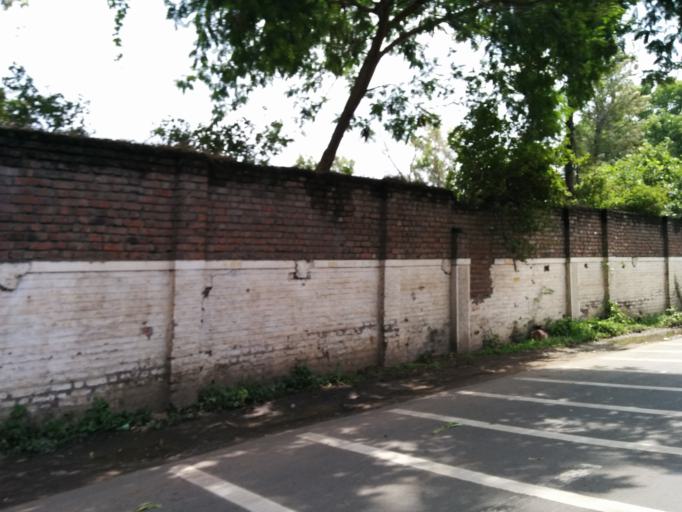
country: IN
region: Maharashtra
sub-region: Pune Division
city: Lohogaon
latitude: 18.5334
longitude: 73.9201
